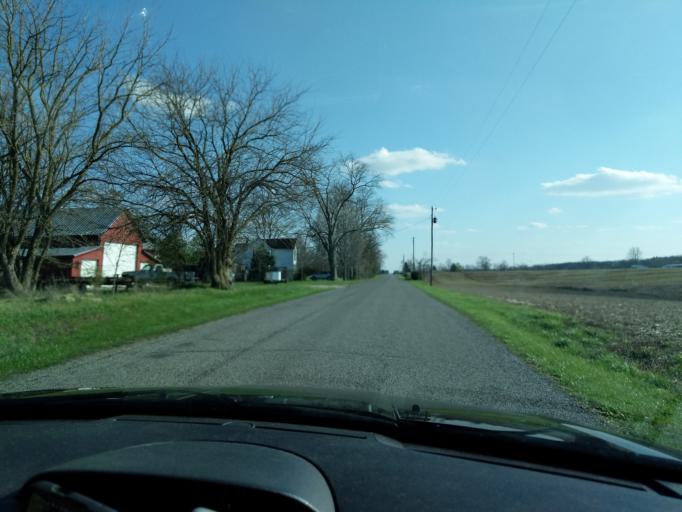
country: US
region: Ohio
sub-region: Champaign County
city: Urbana
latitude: 40.1592
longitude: -83.8329
